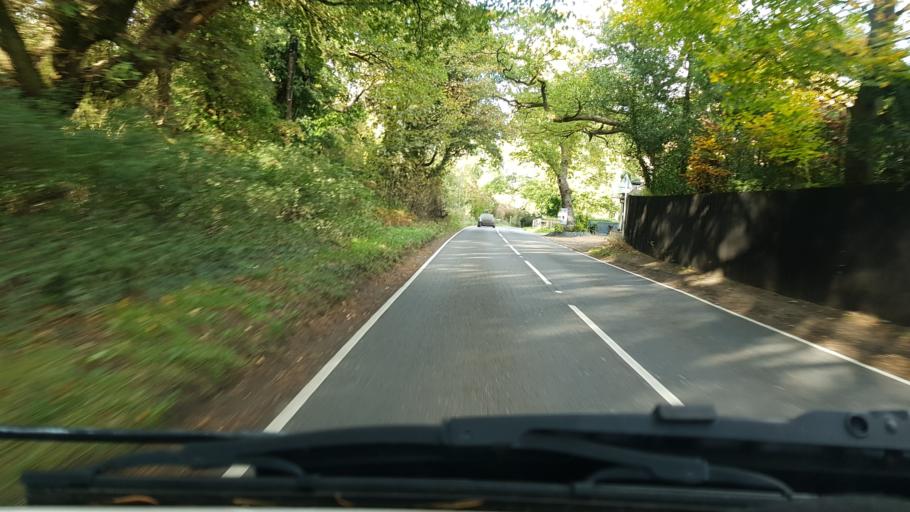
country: GB
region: England
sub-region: Surrey
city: Chilworth
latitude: 51.2359
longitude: -0.5064
